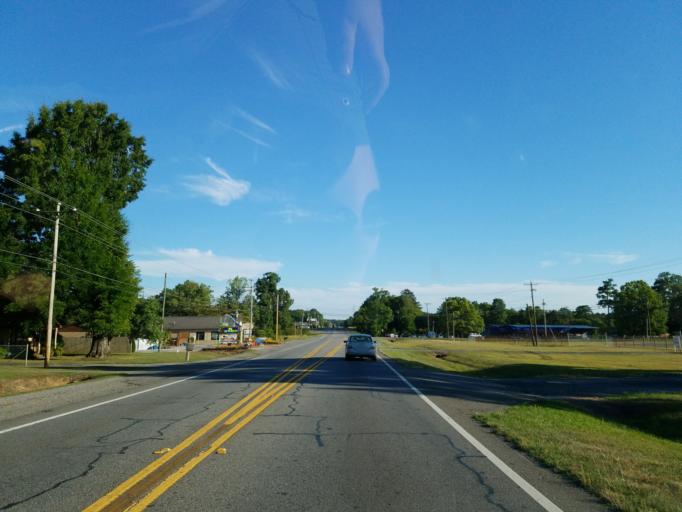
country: US
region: Georgia
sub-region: Gordon County
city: Calhoun
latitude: 34.4752
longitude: -84.9345
